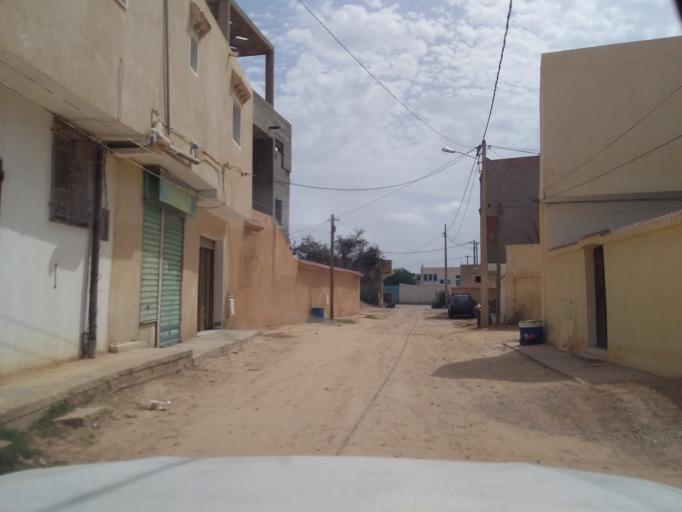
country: TN
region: Qabis
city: Matmata
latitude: 33.6142
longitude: 10.2927
